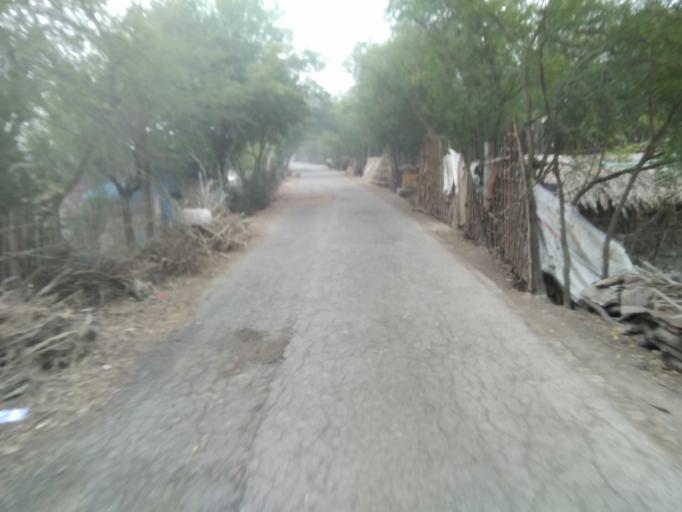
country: BD
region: Khulna
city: Satkhira
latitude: 22.5798
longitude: 89.0694
